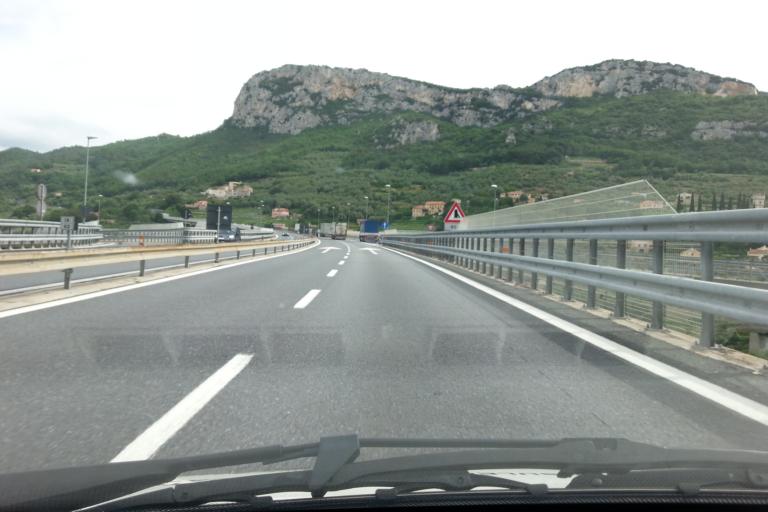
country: IT
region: Liguria
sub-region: Provincia di Savona
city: Calice Ligure
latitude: 44.1854
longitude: 8.3041
